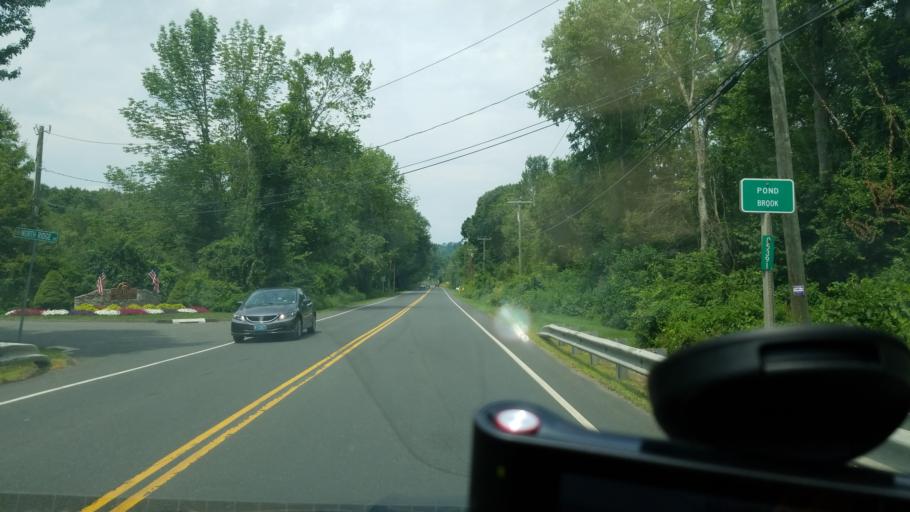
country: US
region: Connecticut
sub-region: Fairfield County
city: Newtown
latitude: 41.4323
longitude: -73.3548
